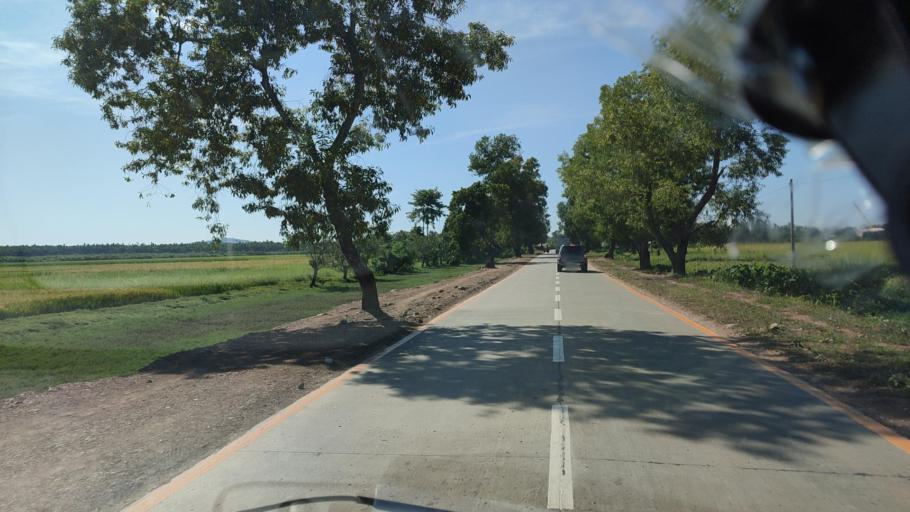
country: MM
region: Rakhine
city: Sittwe
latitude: 20.4781
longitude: 93.2733
